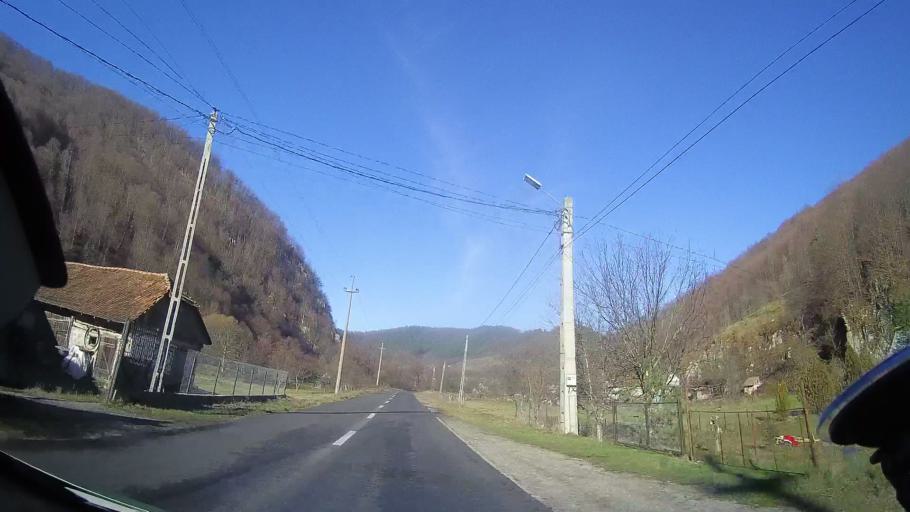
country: RO
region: Bihor
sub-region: Comuna Bulz
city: Bulz
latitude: 46.9182
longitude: 22.6552
